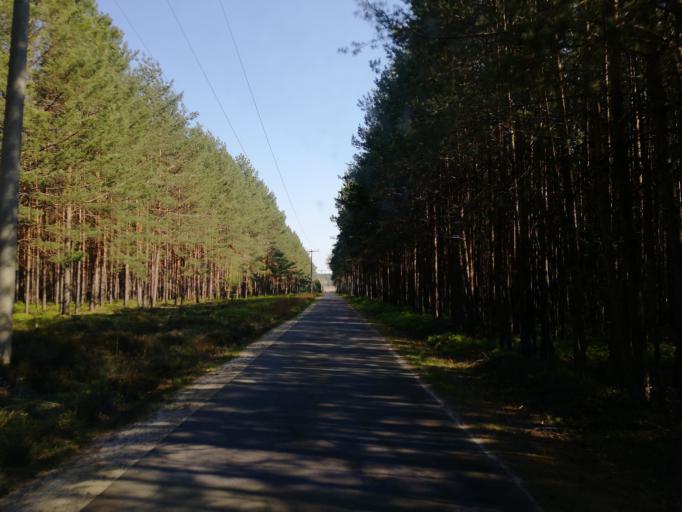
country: DE
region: Brandenburg
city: Bronkow
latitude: 51.6572
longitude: 13.8561
